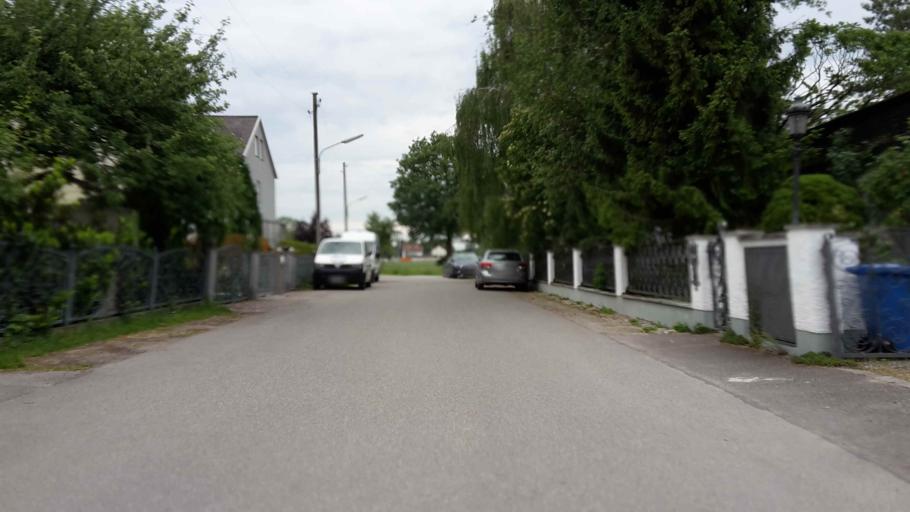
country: DE
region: Bavaria
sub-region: Upper Bavaria
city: Grobenzell
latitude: 48.1804
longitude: 11.4175
